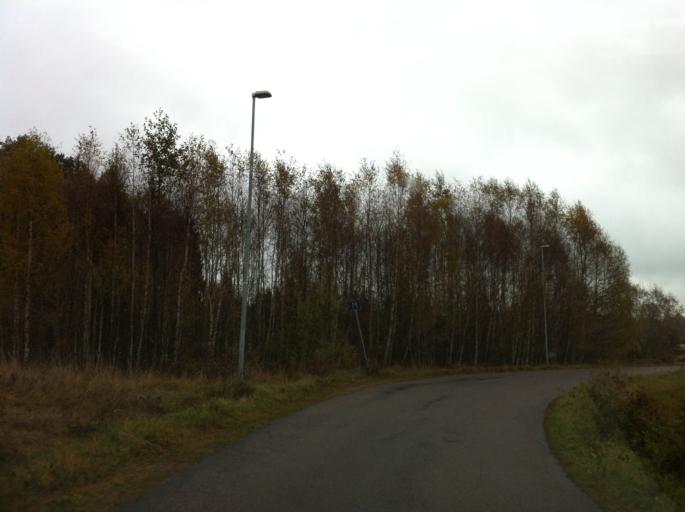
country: SE
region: Uppsala
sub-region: Osthammars Kommun
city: OEsthammar
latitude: 60.2663
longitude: 18.3460
